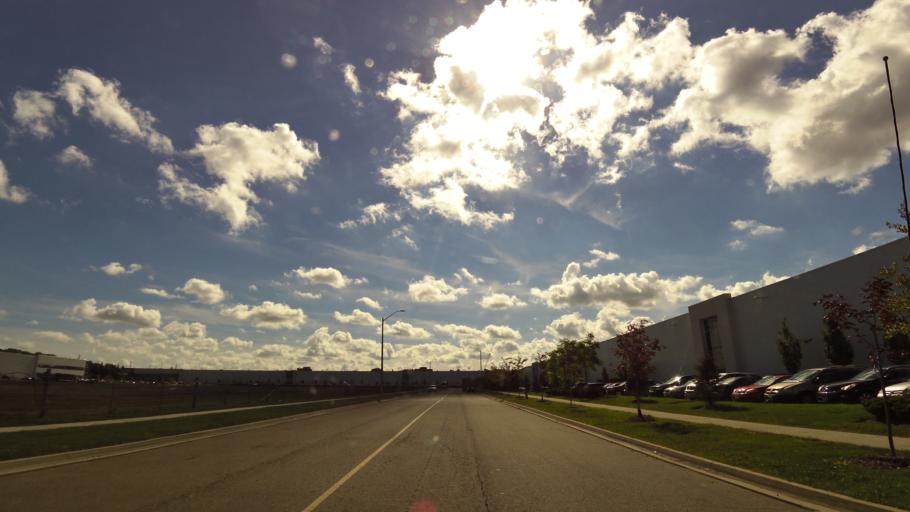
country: CA
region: Ontario
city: Mississauga
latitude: 43.5848
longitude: -79.7314
